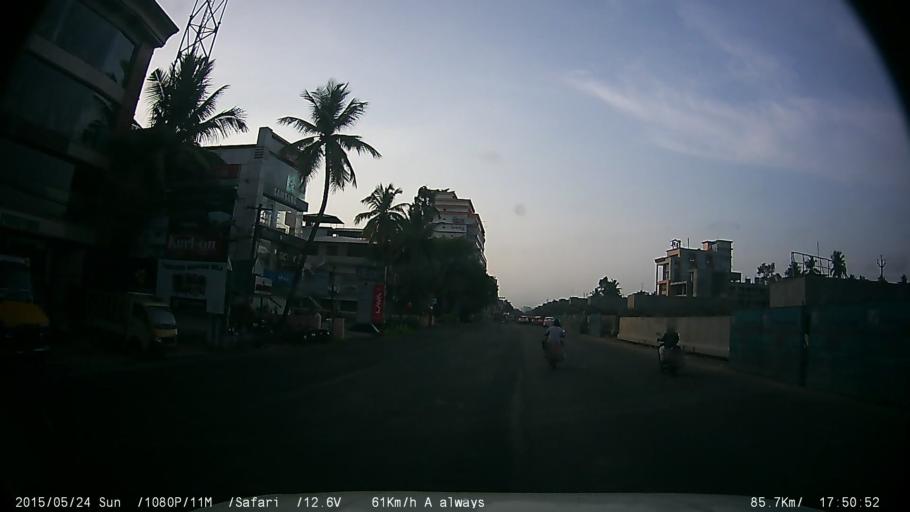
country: IN
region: Kerala
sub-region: Ernakulam
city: Elur
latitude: 10.0031
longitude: 76.3133
